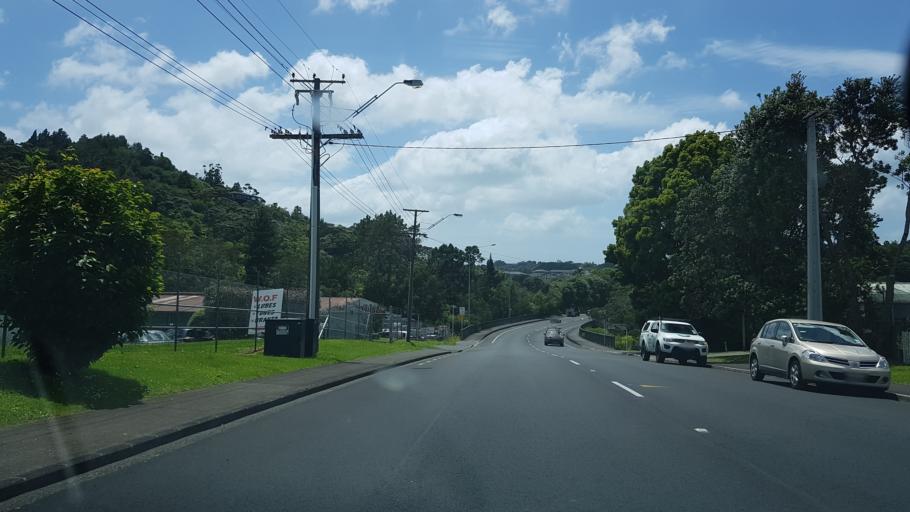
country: NZ
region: Auckland
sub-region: Auckland
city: North Shore
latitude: -36.7866
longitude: 174.7026
